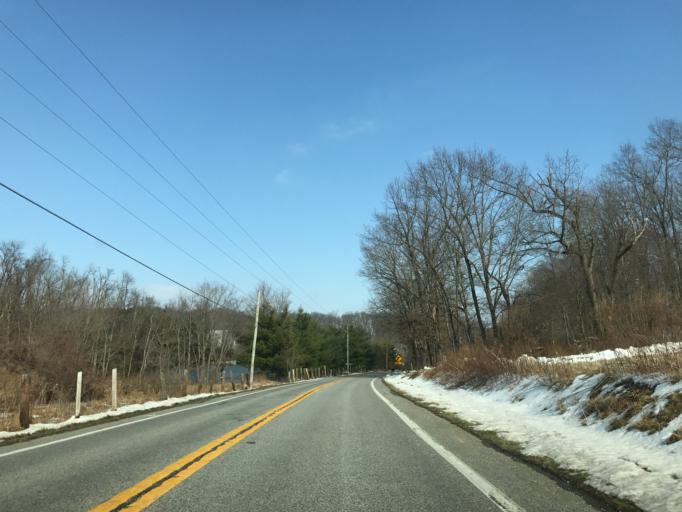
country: US
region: Pennsylvania
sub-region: York County
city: Stewartstown
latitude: 39.7036
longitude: -76.5194
